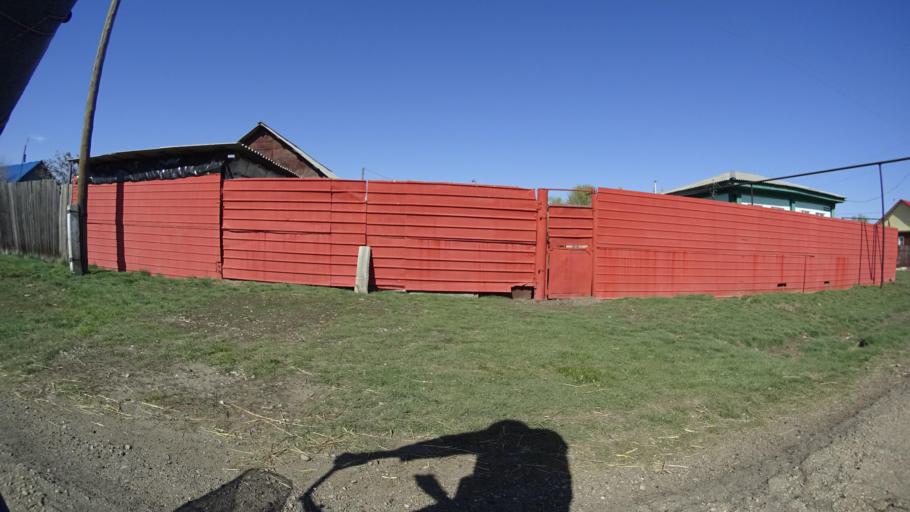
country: RU
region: Chelyabinsk
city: Chesma
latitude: 53.7975
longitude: 61.0234
